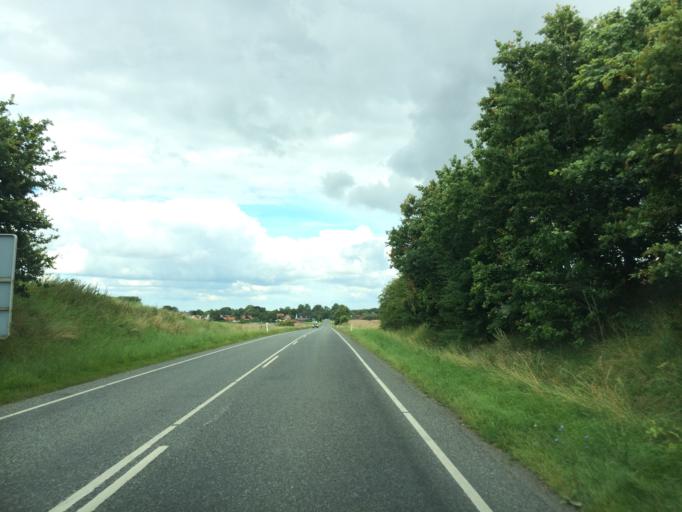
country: DK
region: South Denmark
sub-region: Assens Kommune
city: Tommerup
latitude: 55.2445
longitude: 10.2226
